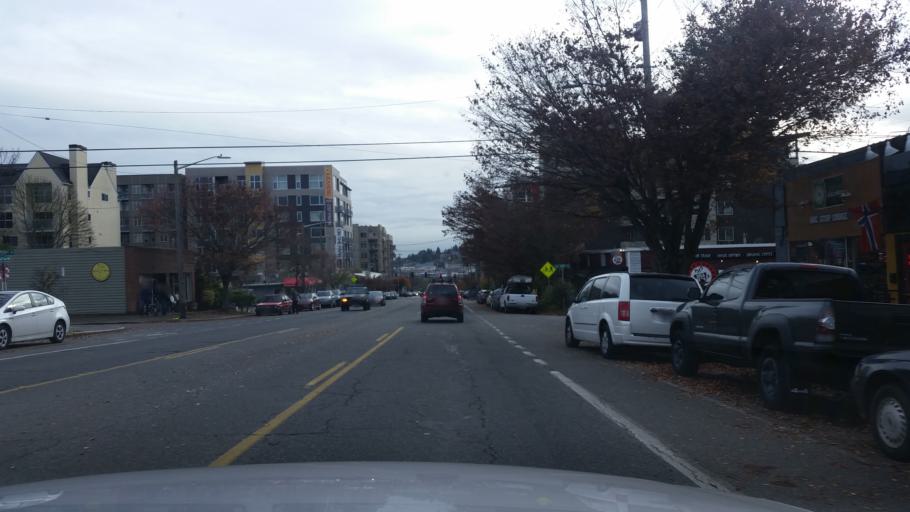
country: US
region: Washington
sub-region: King County
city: Seattle
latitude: 47.6721
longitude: -122.3876
